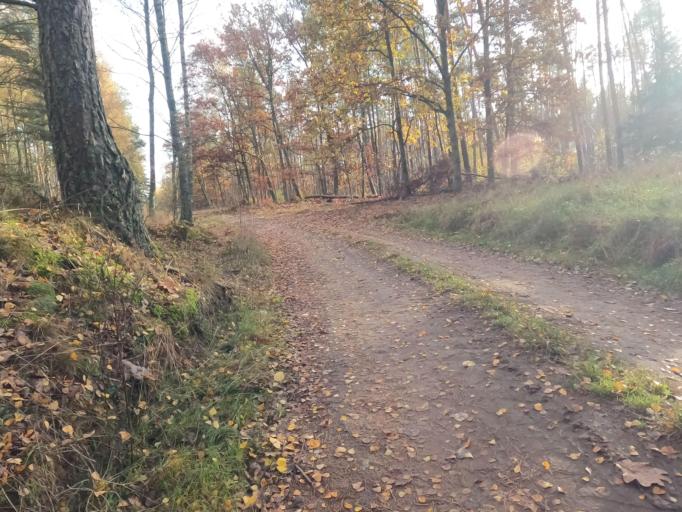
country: PL
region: West Pomeranian Voivodeship
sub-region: Powiat szczecinecki
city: Lubowo
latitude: 53.5500
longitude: 16.4240
